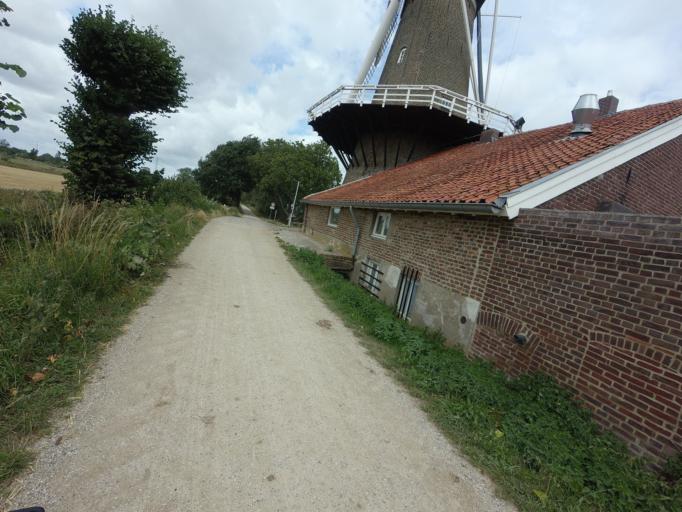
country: NL
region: Limburg
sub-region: Gemeente Maasgouw
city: Maasbracht
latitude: 51.1203
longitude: 5.8363
